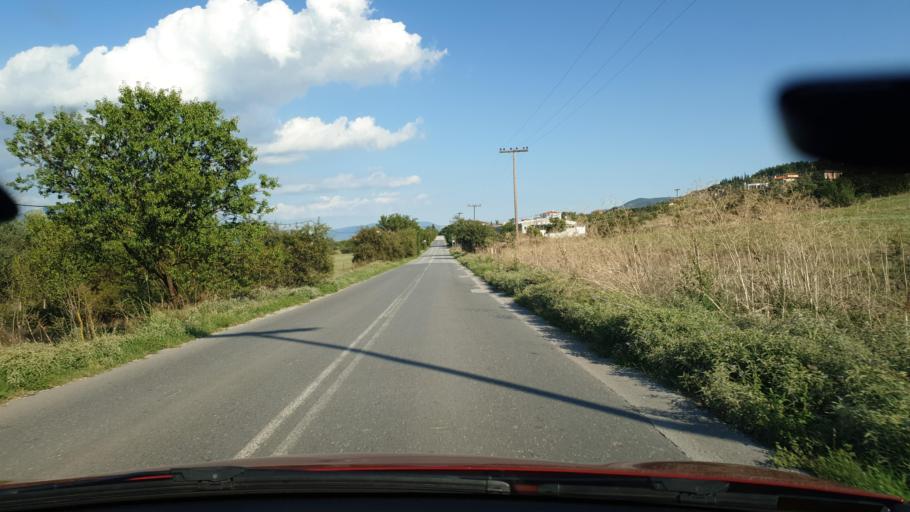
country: GR
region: Central Macedonia
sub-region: Nomos Thessalonikis
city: Agia Paraskevi
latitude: 40.4818
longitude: 23.0624
